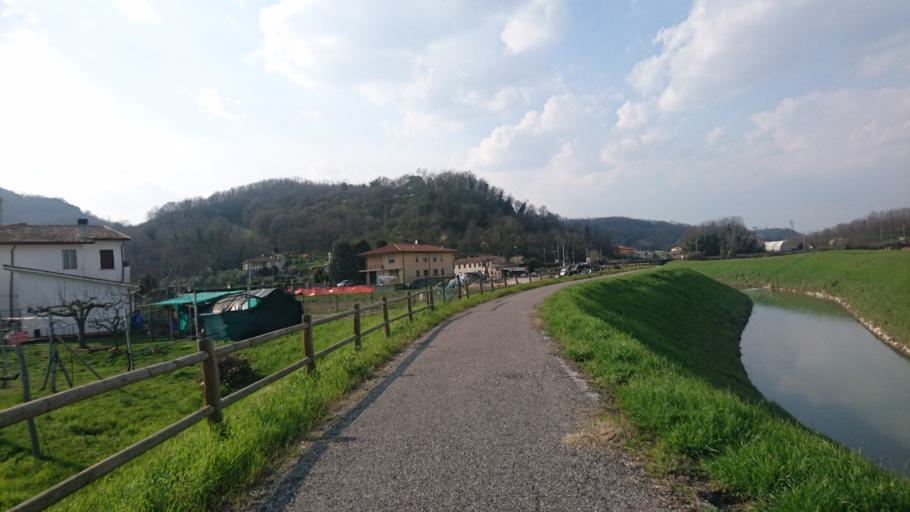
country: IT
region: Veneto
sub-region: Provincia di Padova
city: Montegrotto Terme
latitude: 45.3105
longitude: 11.7906
